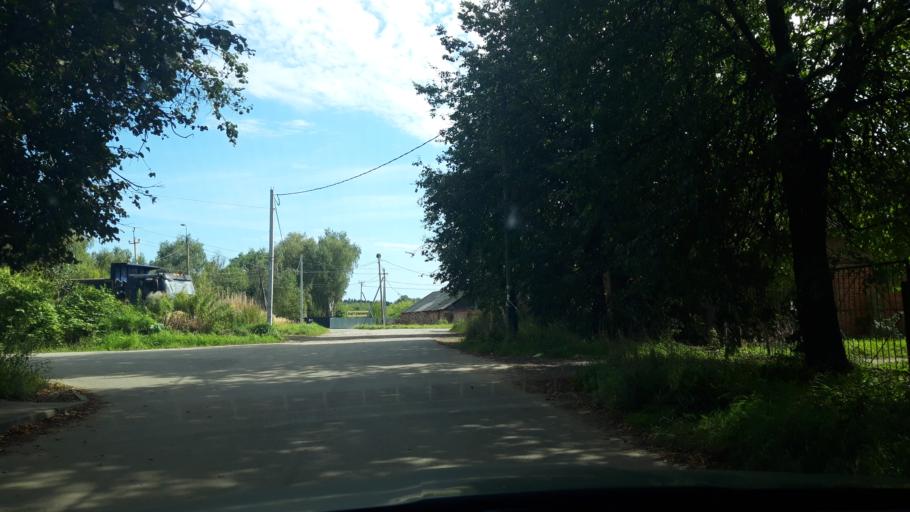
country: RU
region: Moskovskaya
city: Chashnikovo
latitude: 56.0342
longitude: 37.1690
